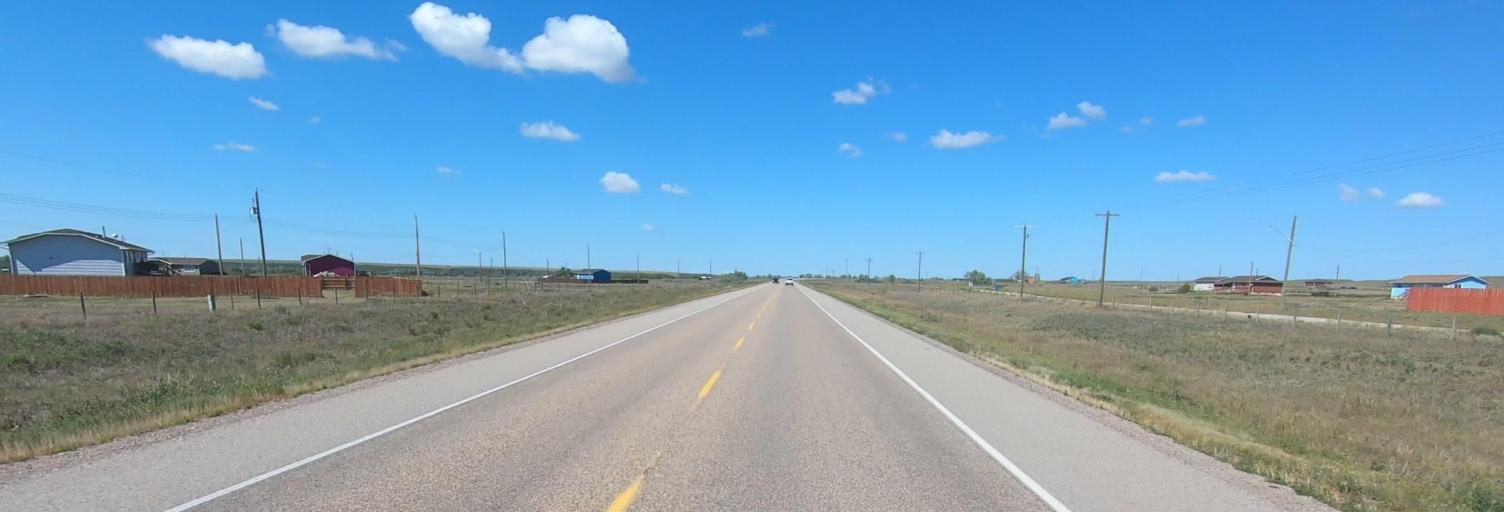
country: CA
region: Alberta
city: Strathmore
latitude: 50.8537
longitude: -113.1215
